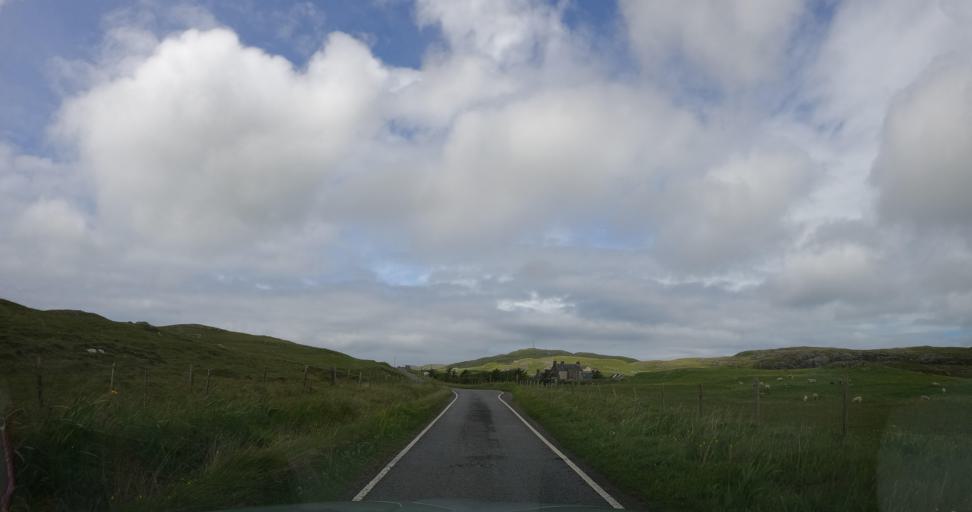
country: GB
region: Scotland
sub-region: Eilean Siar
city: Barra
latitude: 57.0018
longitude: -7.4874
